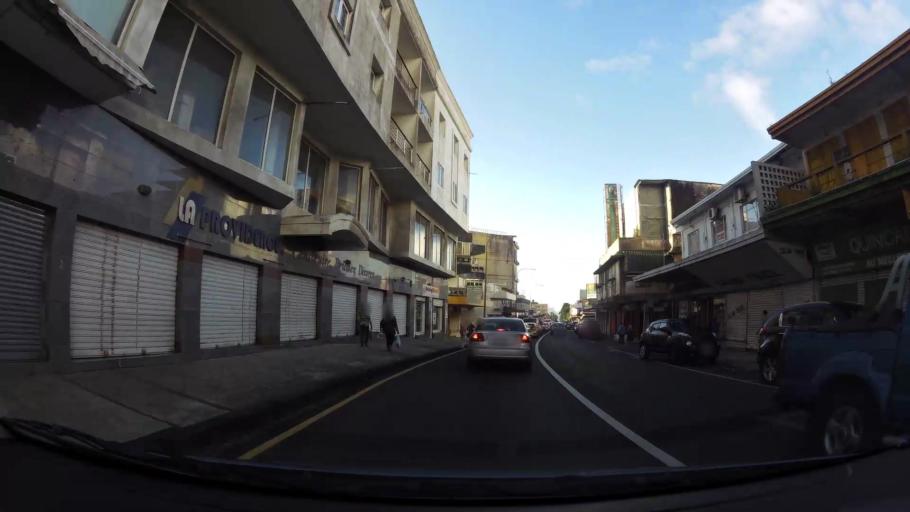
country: MU
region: Plaines Wilhems
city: Curepipe
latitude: -20.3157
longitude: 57.5231
